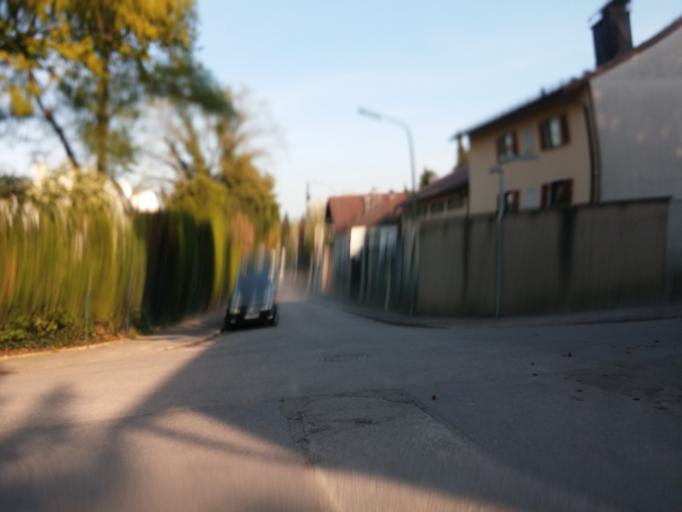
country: DE
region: Bavaria
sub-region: Upper Bavaria
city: Neubiberg
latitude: 48.1104
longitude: 11.6635
